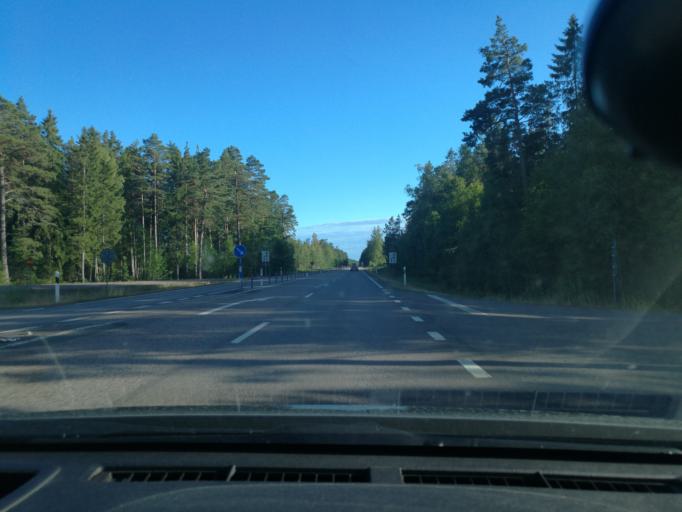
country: SE
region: Kalmar
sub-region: Monsteras Kommun
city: Timmernabben
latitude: 57.0064
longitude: 16.4204
